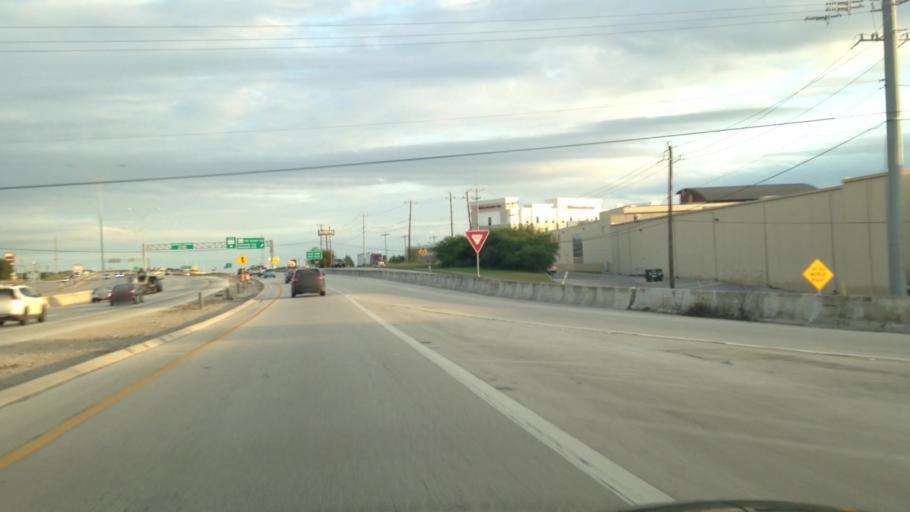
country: US
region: Texas
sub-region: Bexar County
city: Live Oak
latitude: 29.5658
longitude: -98.3317
